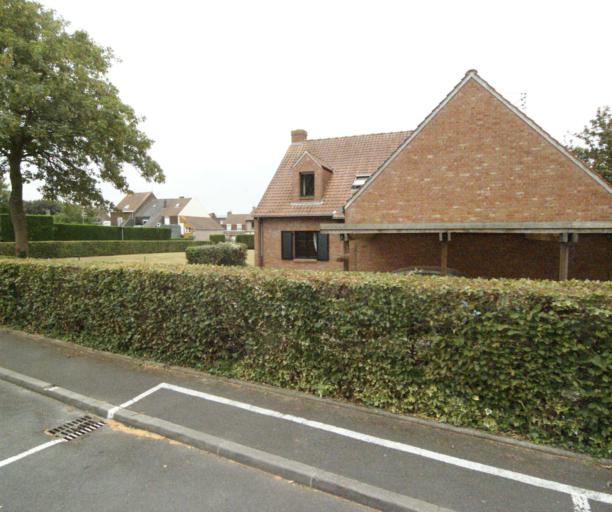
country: FR
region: Nord-Pas-de-Calais
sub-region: Departement du Nord
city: Bondues
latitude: 50.7020
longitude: 3.0942
